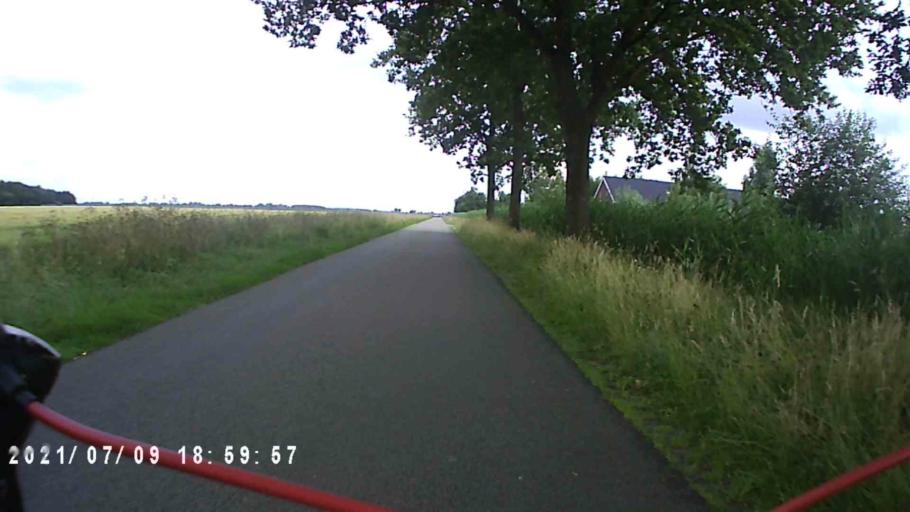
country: NL
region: Groningen
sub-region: Gemeente Veendam
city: Veendam
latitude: 53.0405
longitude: 6.9000
